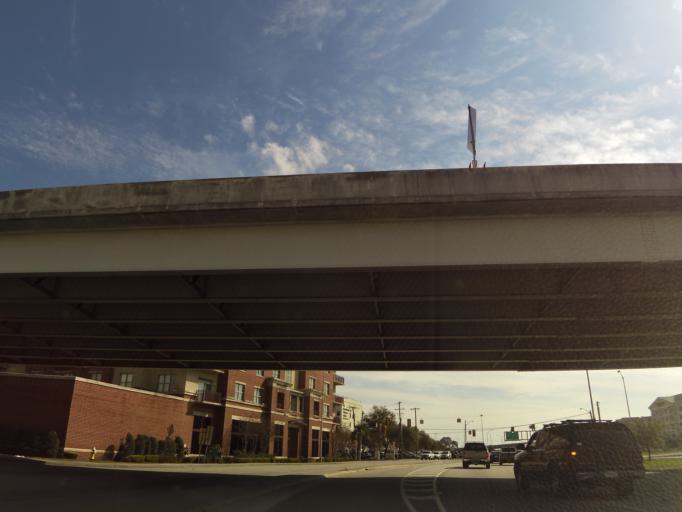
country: US
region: South Carolina
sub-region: Charleston County
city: Charleston
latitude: 32.7855
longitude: -79.9563
